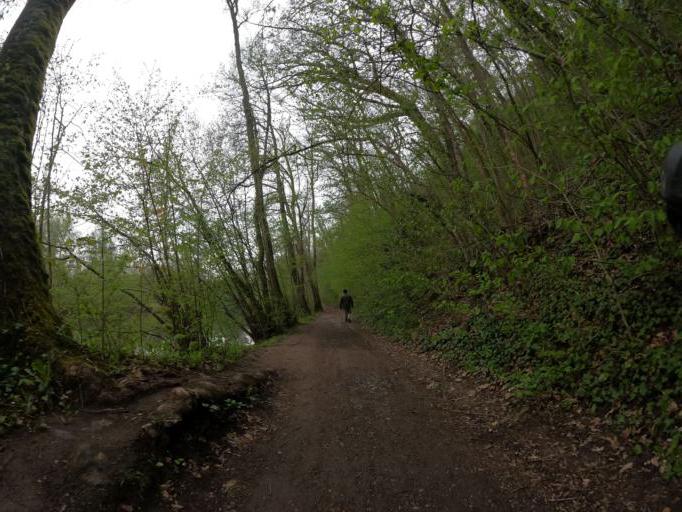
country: DE
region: Baden-Wuerttemberg
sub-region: Regierungsbezirk Stuttgart
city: Markgroningen
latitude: 48.9292
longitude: 9.0834
